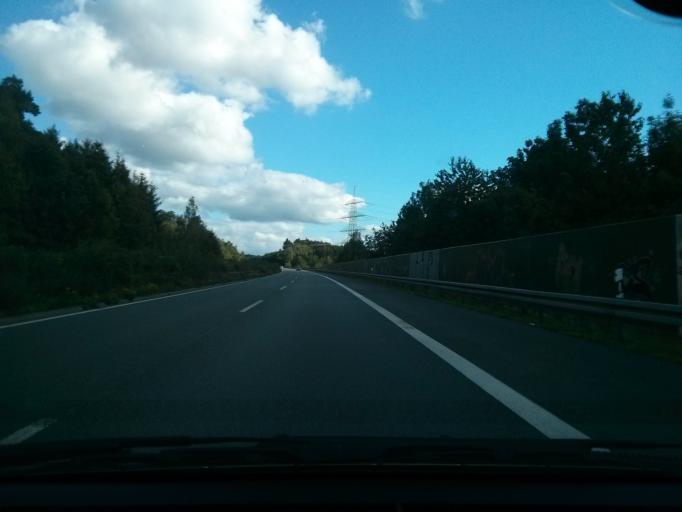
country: DE
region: North Rhine-Westphalia
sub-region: Regierungsbezirk Arnsberg
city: Arnsberg
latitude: 51.4335
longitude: 8.0083
